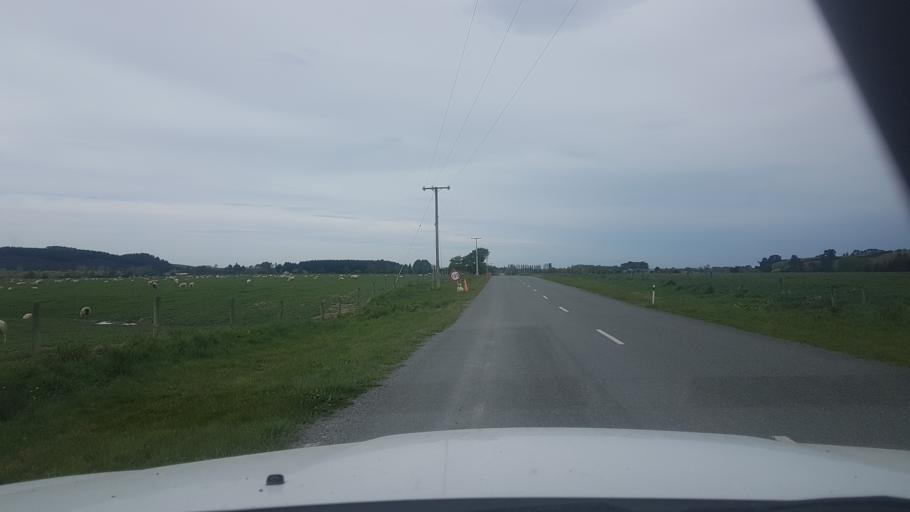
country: NZ
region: Canterbury
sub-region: Timaru District
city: Pleasant Point
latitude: -44.0848
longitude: 171.1823
